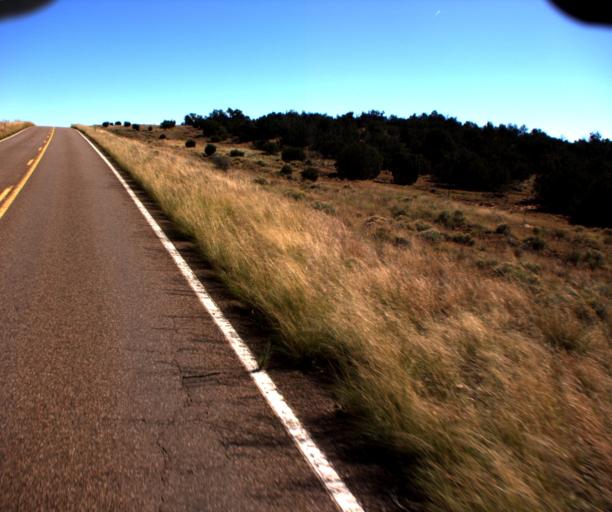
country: US
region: Arizona
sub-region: Navajo County
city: Heber-Overgaard
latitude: 34.4574
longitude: -110.4402
